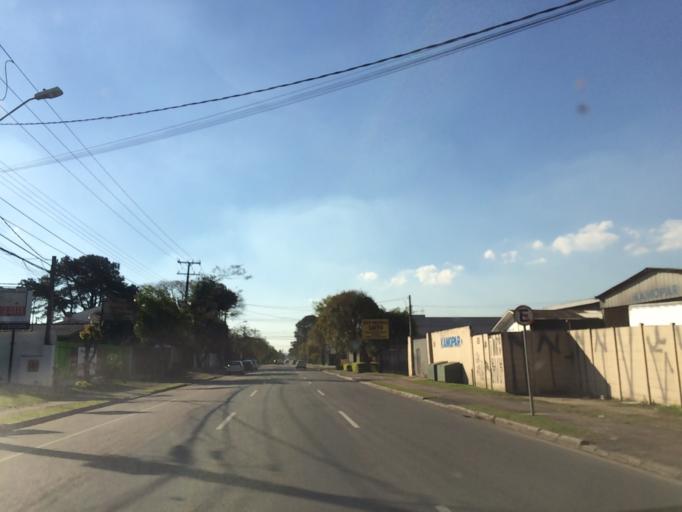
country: BR
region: Parana
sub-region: Sao Jose Dos Pinhais
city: Sao Jose dos Pinhais
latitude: -25.4927
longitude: -49.2405
